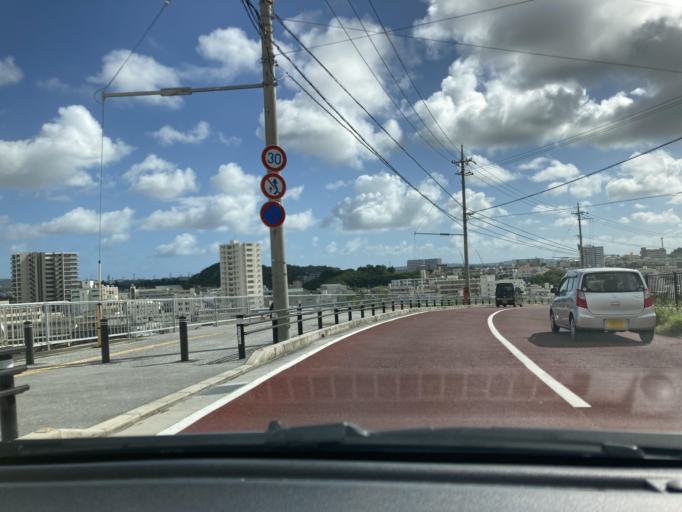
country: JP
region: Okinawa
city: Tomigusuku
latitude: 26.1998
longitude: 127.7297
